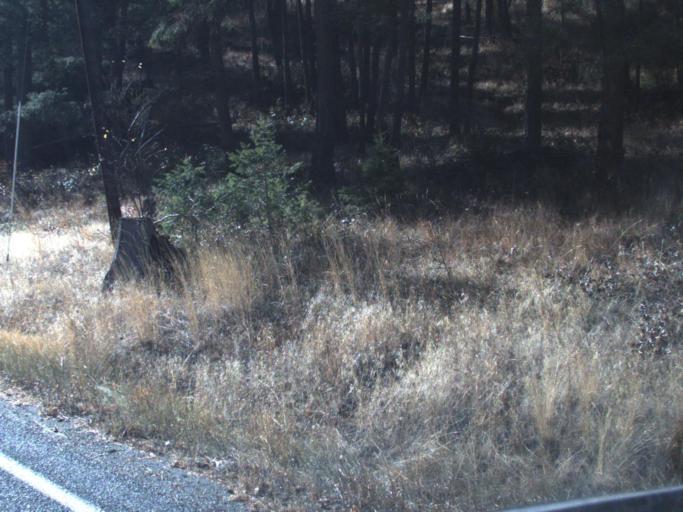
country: CA
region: British Columbia
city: Grand Forks
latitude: 48.9221
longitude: -118.5656
